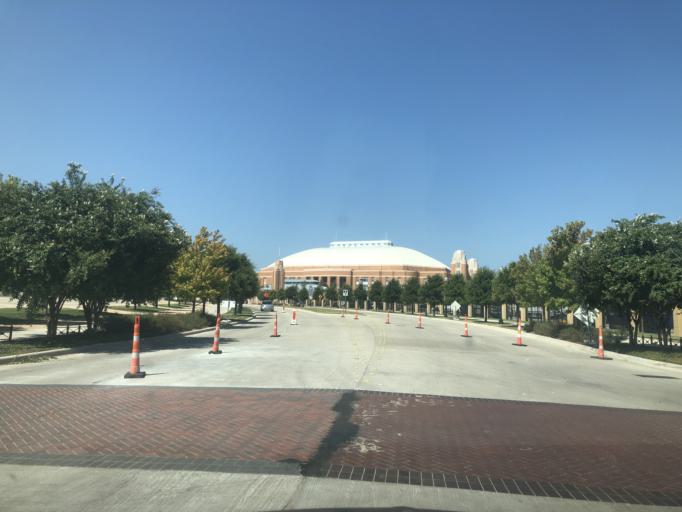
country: US
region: Texas
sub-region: Tarrant County
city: River Oaks
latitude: 32.7423
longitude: -97.3644
